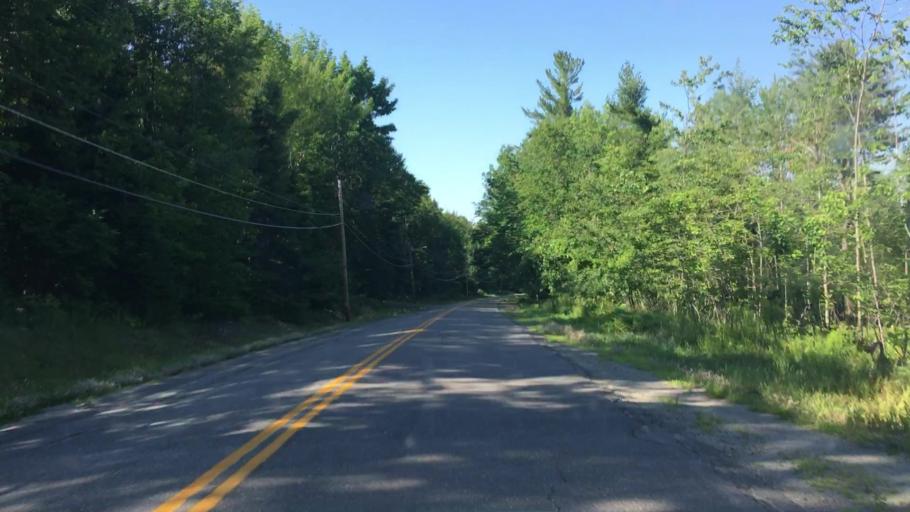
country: US
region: Maine
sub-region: Penobscot County
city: Enfield
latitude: 45.2678
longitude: -68.5618
